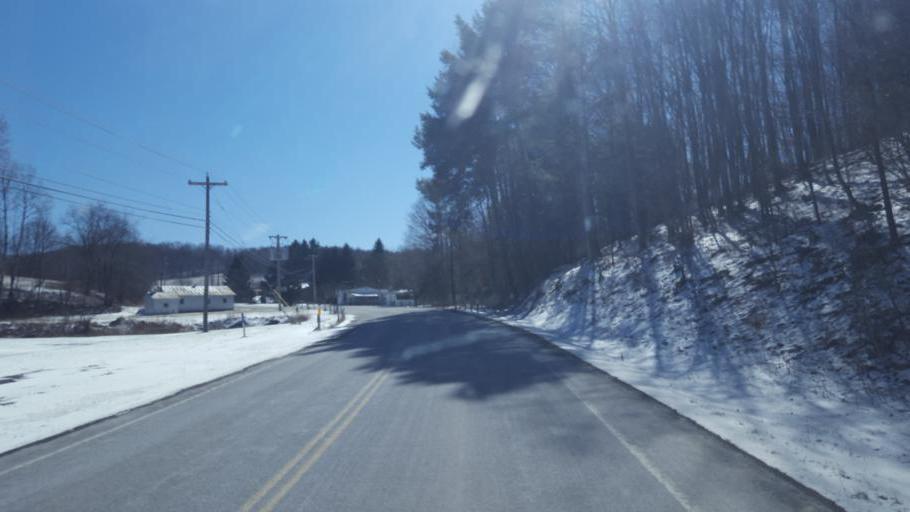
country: US
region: New York
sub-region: Allegany County
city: Andover
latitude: 42.0675
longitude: -77.8379
